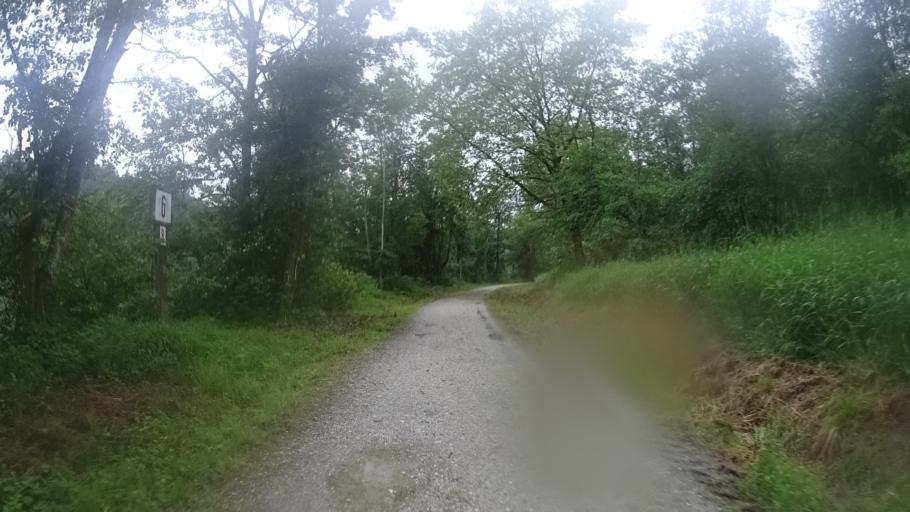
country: DE
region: Bavaria
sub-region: Lower Bavaria
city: Passau
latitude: 48.5338
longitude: 13.4484
